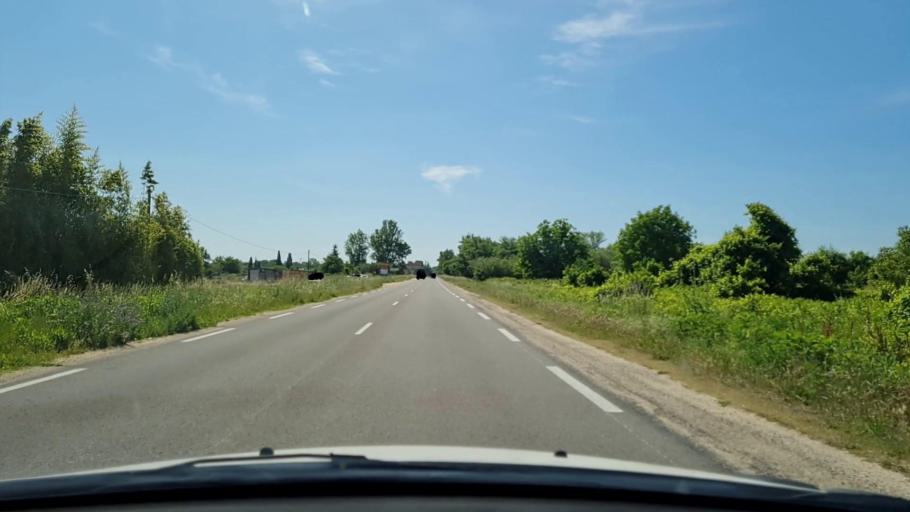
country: FR
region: Languedoc-Roussillon
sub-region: Departement du Gard
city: Moussac
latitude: 43.9663
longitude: 4.2279
